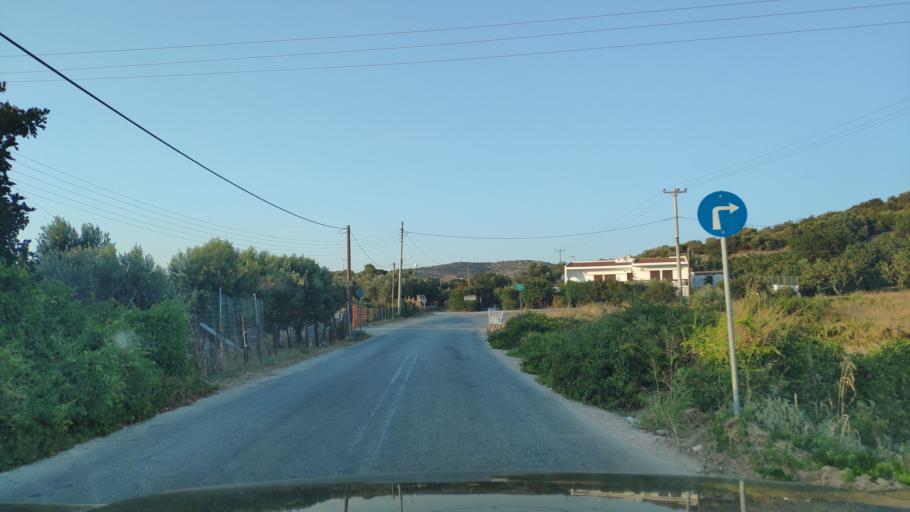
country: GR
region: Attica
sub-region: Nomarchia Anatolikis Attikis
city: Artemida
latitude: 37.9283
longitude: 23.9796
